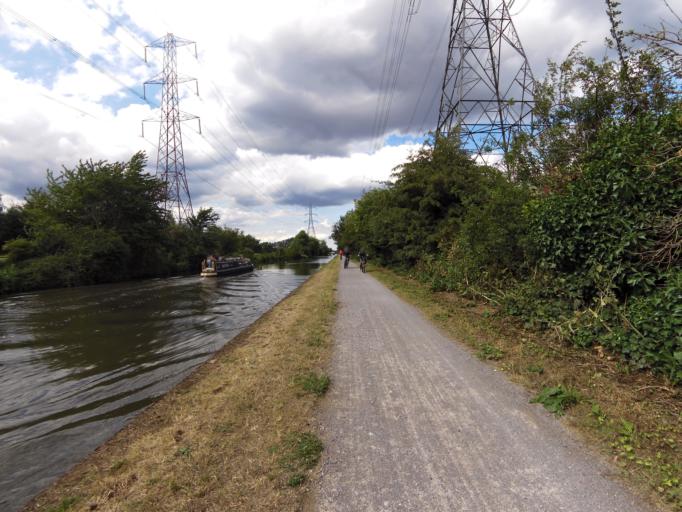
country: GB
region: England
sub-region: Greater London
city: Walthamstow
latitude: 51.6332
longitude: -0.0304
